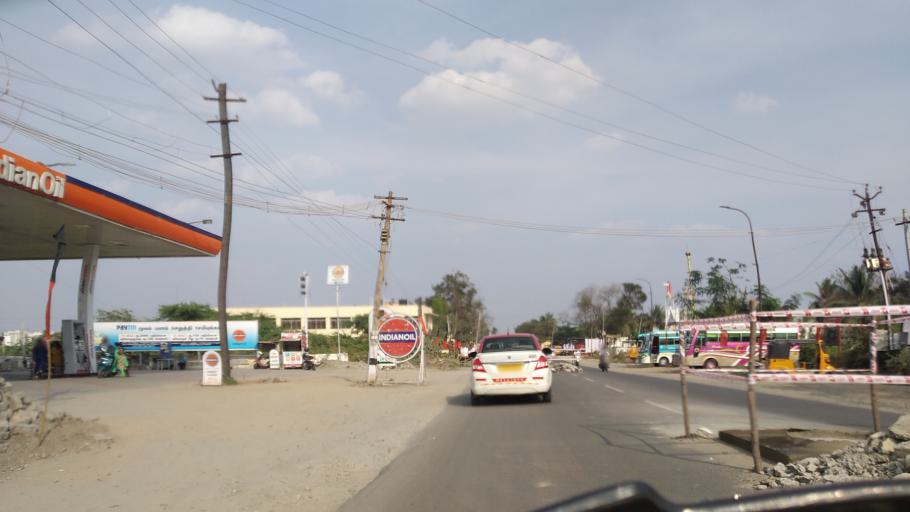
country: IN
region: Tamil Nadu
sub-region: Coimbatore
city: Perur
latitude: 10.9839
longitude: 76.9287
